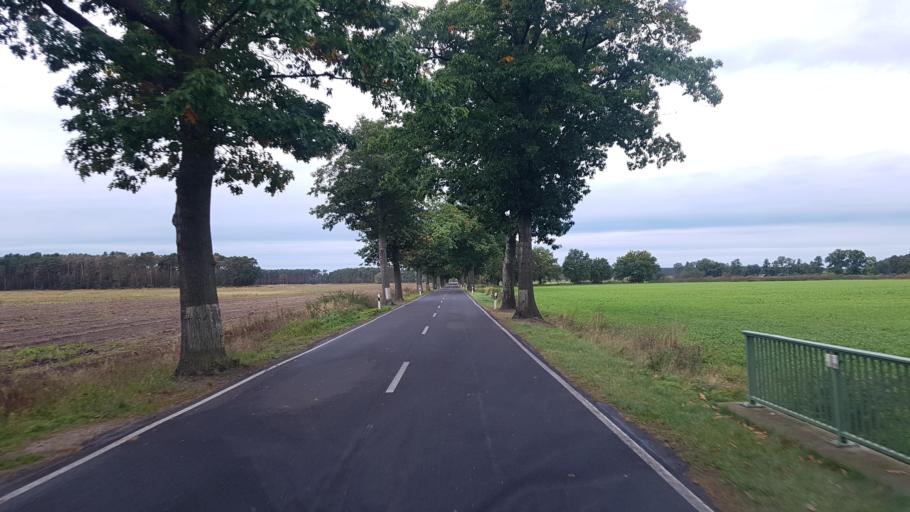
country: DE
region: Brandenburg
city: Kasel-Golzig
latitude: 51.9350
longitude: 13.6718
